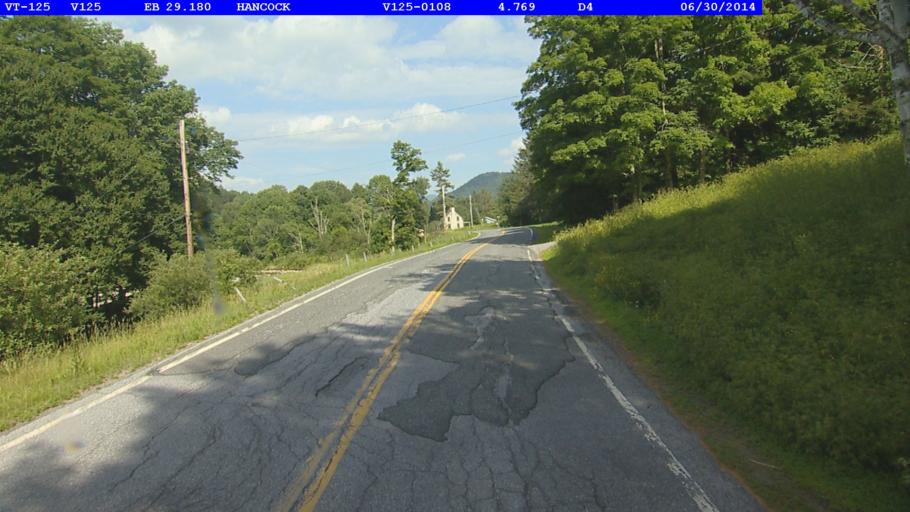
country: US
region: Vermont
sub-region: Orange County
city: Randolph
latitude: 43.9281
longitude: -72.8879
